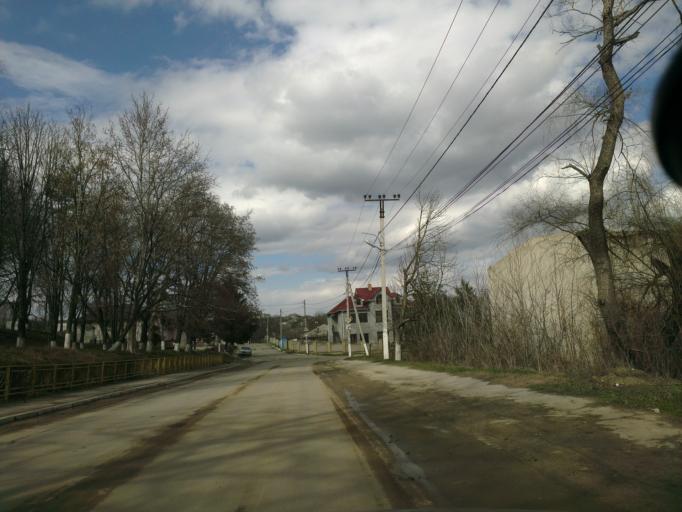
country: MD
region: Hincesti
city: Hincesti
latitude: 46.8252
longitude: 28.5851
